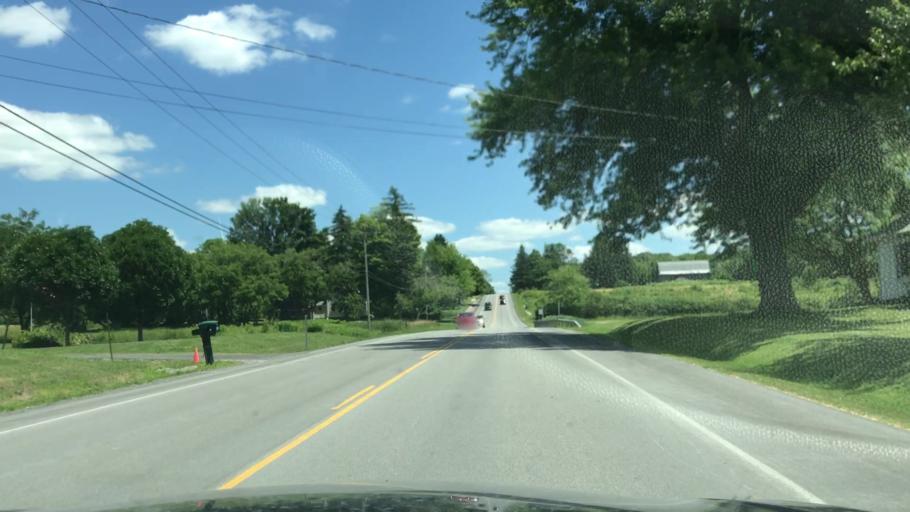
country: US
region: New York
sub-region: Erie County
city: Alden
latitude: 42.7697
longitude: -78.4356
